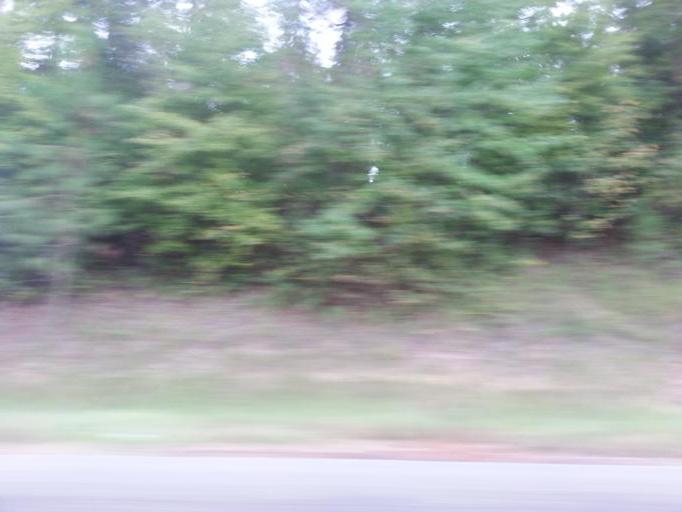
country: US
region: Alabama
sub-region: Butler County
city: Georgiana
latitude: 31.6096
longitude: -86.8168
